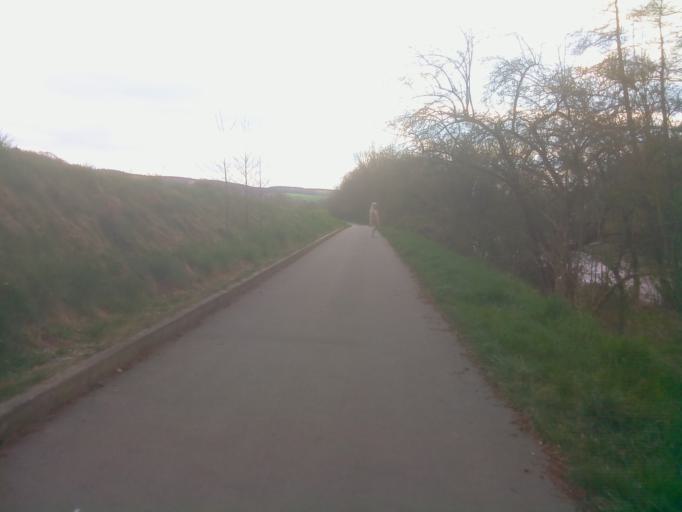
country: DE
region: Thuringia
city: Kahla
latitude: 50.7965
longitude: 11.5884
